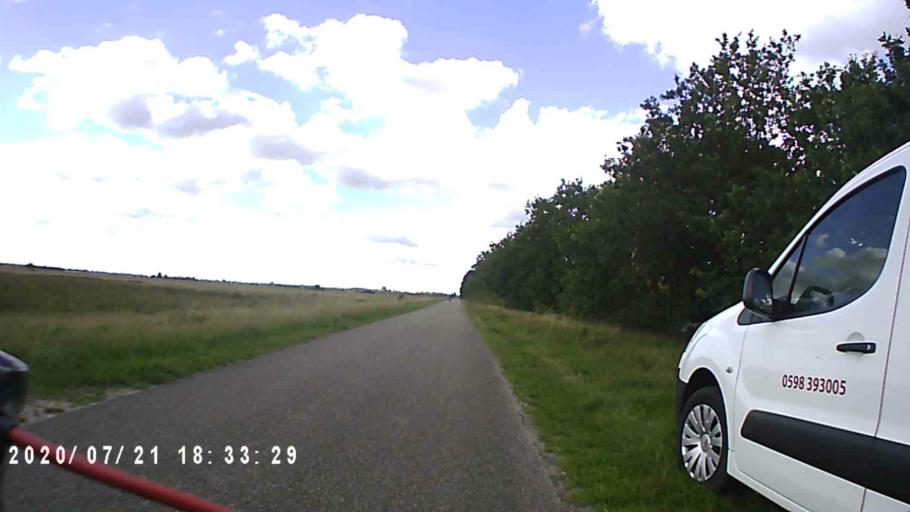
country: NL
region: Groningen
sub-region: Gemeente Hoogezand-Sappemeer
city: Hoogezand
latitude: 53.1858
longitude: 6.7391
